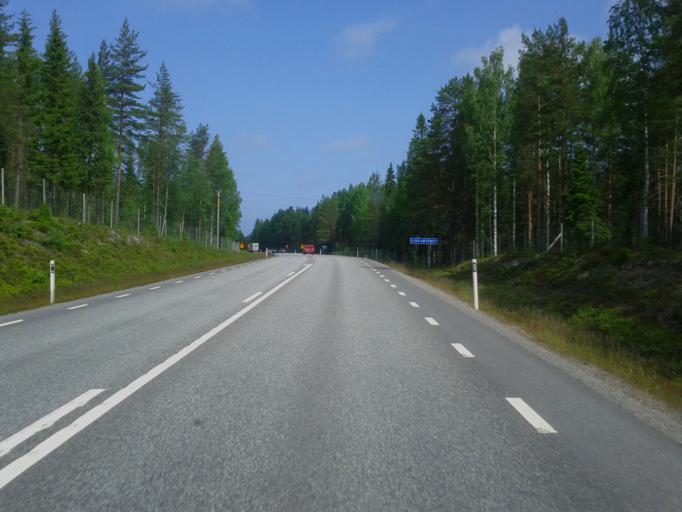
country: SE
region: Vaesterbotten
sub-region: Skelleftea Kommun
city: Burea
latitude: 64.5340
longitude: 21.2589
